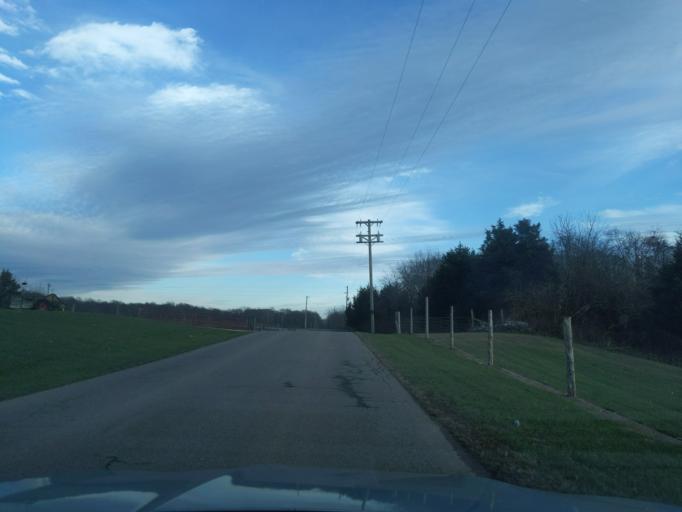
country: US
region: Indiana
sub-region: Decatur County
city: Westport
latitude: 39.2338
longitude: -85.5448
